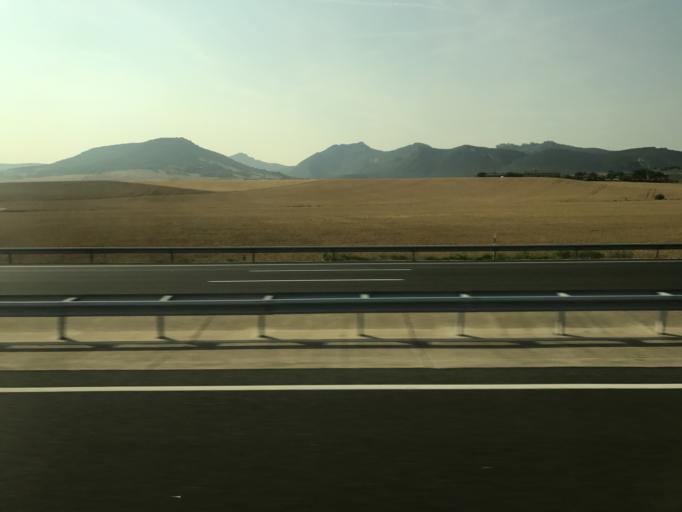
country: ES
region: Castille and Leon
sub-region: Provincia de Burgos
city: Bugedo
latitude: 42.6718
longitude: -3.0279
